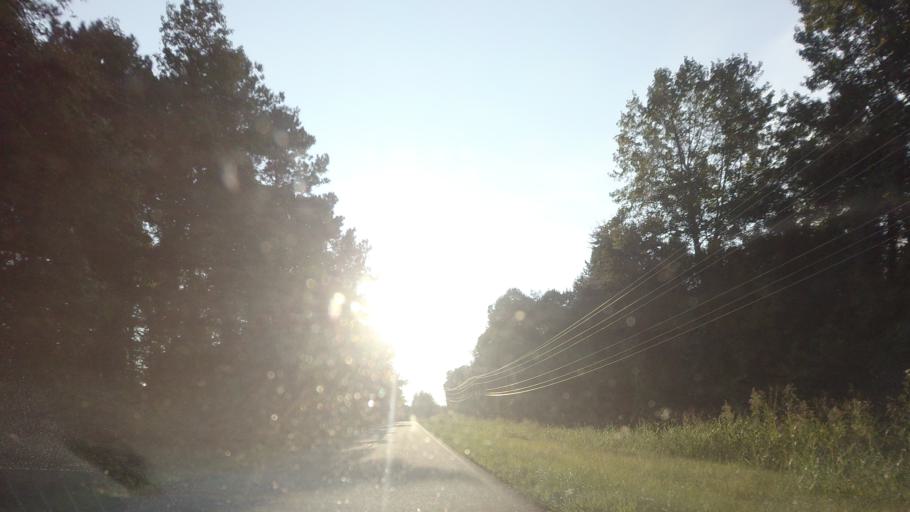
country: US
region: Georgia
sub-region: Bibb County
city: West Point
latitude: 32.9405
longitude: -83.7718
